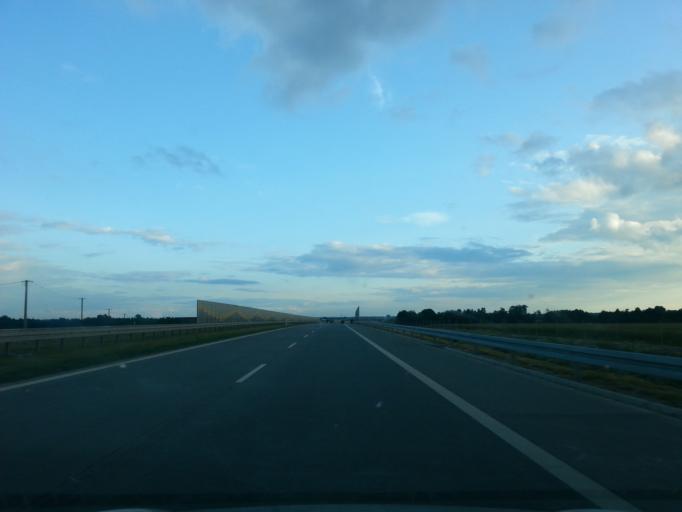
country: PL
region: Lodz Voivodeship
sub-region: Powiat sieradzki
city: Brzeznio
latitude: 51.4955
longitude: 18.6852
